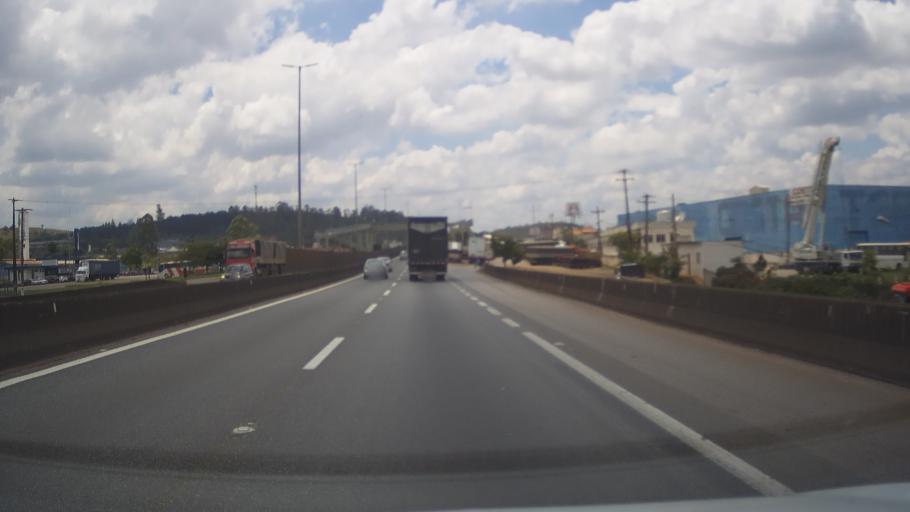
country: BR
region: Minas Gerais
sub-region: Tres Coracoes
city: Tres Coracoes
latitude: -21.6712
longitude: -45.3318
